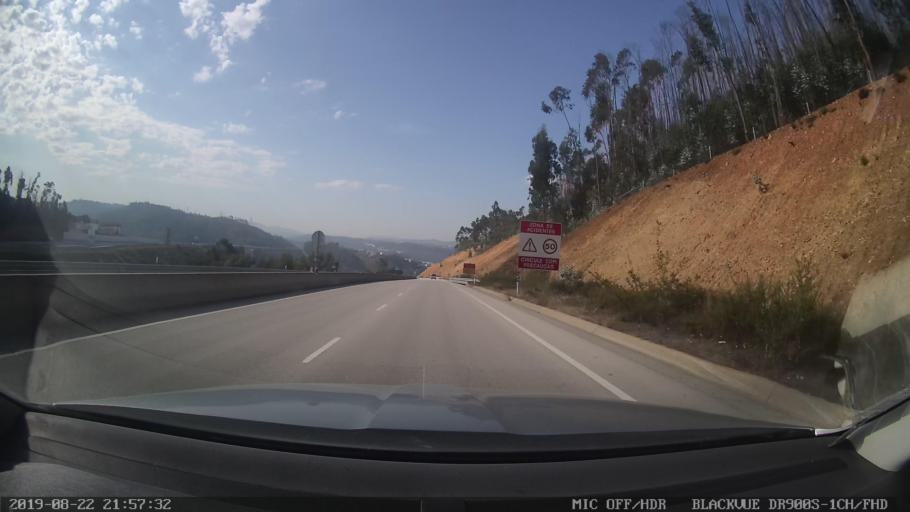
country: PT
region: Coimbra
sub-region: Coimbra
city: Coimbra
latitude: 40.1820
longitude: -8.3808
